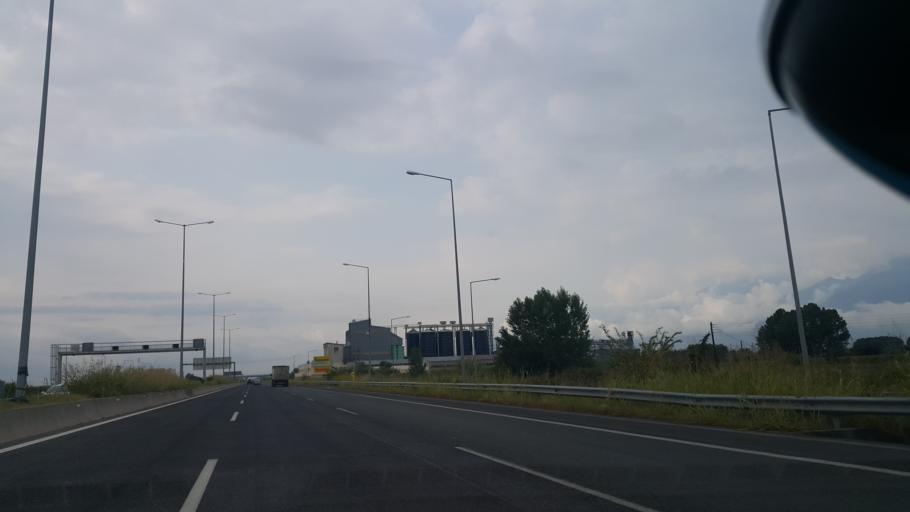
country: GR
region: Central Macedonia
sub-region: Nomos Pierias
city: Peristasi
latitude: 40.2508
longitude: 22.5328
